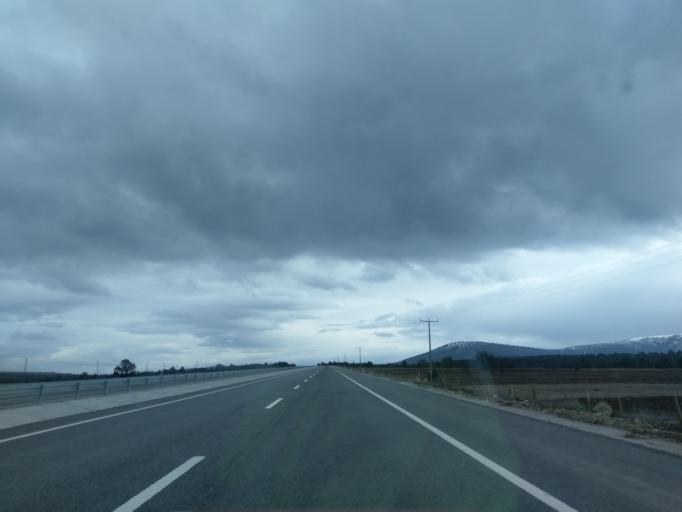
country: TR
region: Kuetahya
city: Cavdarhisar
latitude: 39.2243
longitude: 29.7255
